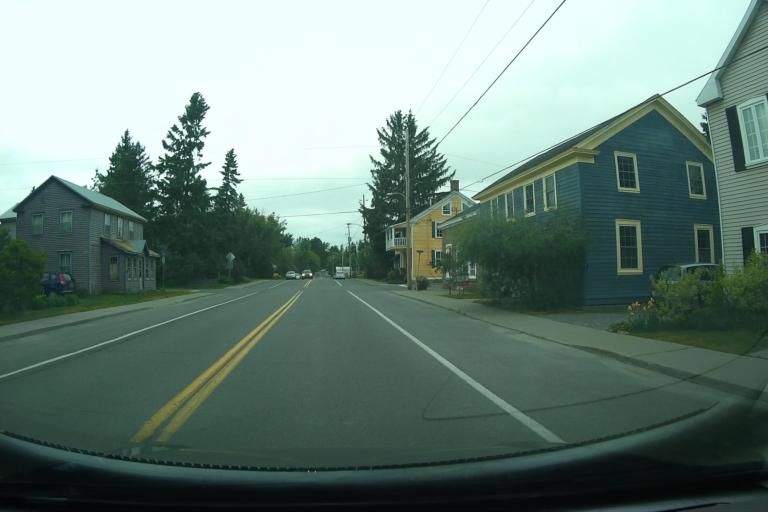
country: CA
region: Ontario
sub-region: Lanark County
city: Smiths Falls
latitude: 44.9820
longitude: -75.7972
